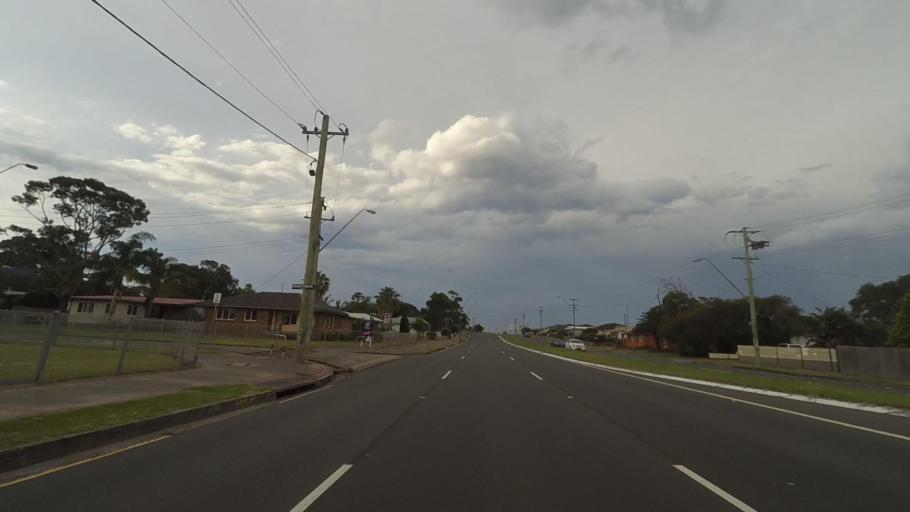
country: AU
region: New South Wales
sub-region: Shellharbour
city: Lake Illawarra
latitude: -34.5507
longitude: 150.8604
